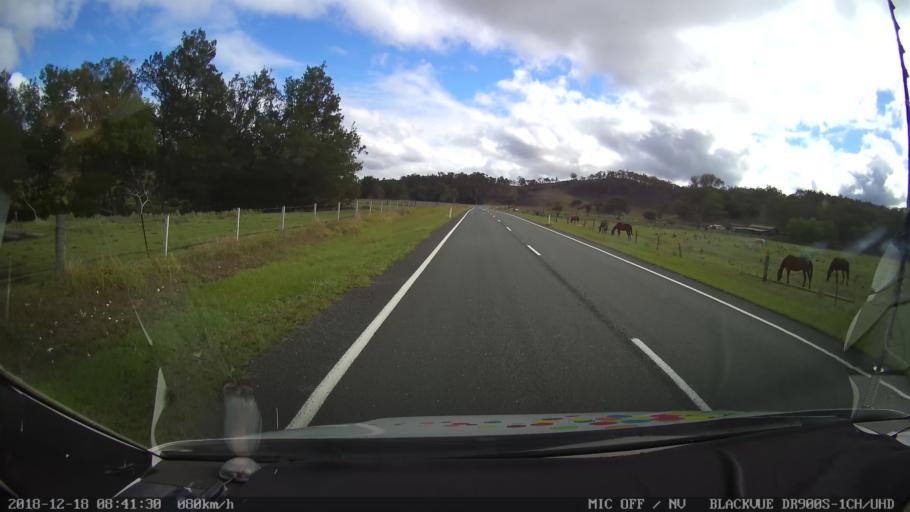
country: AU
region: Queensland
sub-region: Logan
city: Cedar Vale
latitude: -28.2358
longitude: 152.8574
